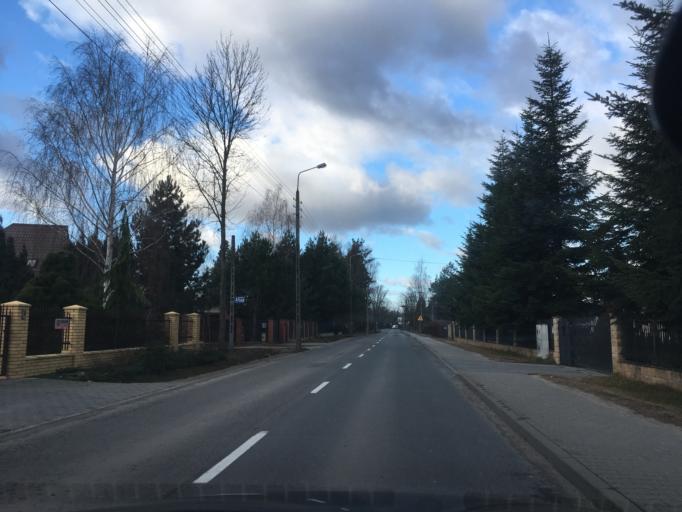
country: PL
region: Masovian Voivodeship
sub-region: Powiat piaseczynski
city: Lesznowola
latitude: 52.0341
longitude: 20.9496
